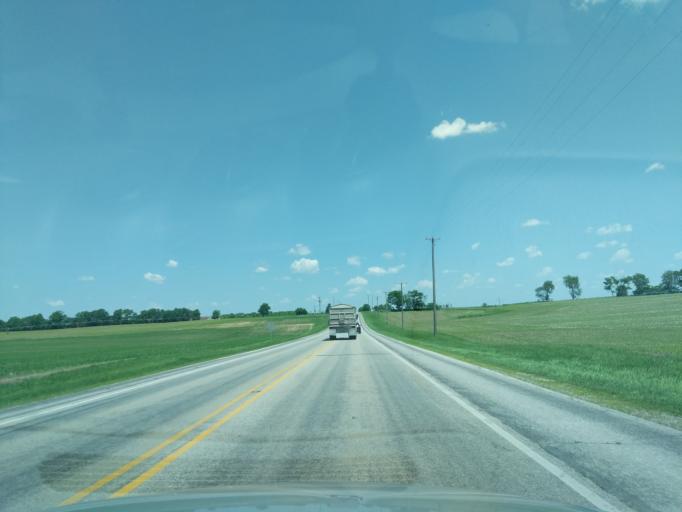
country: US
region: Indiana
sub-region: Noble County
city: Ligonier
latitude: 41.4832
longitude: -85.5774
